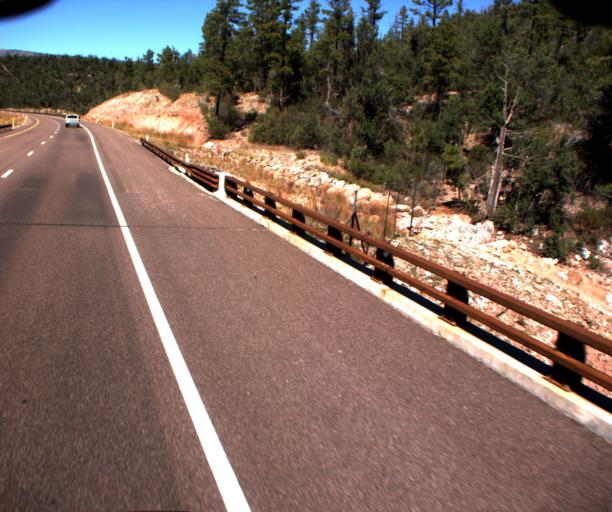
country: US
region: Arizona
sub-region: Gila County
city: Star Valley
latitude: 34.3198
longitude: -111.0645
